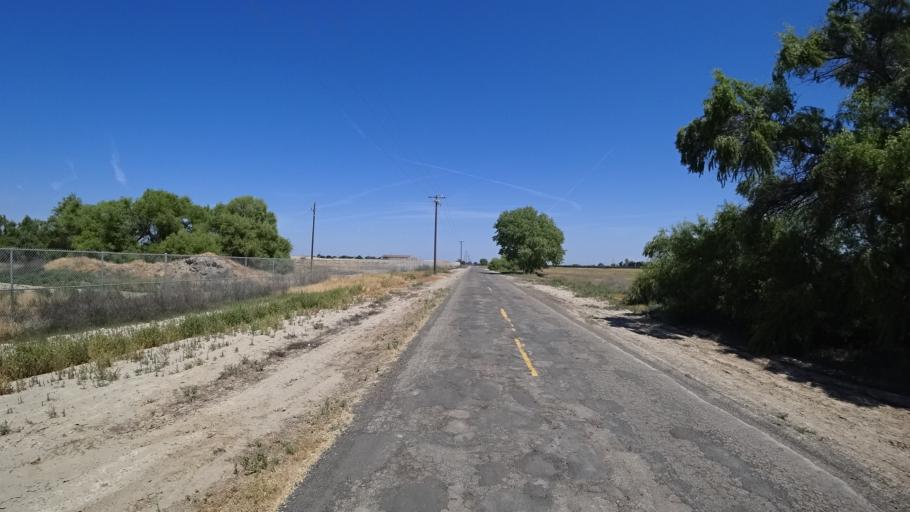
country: US
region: California
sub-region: Kings County
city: Lemoore
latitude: 36.2358
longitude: -119.7446
